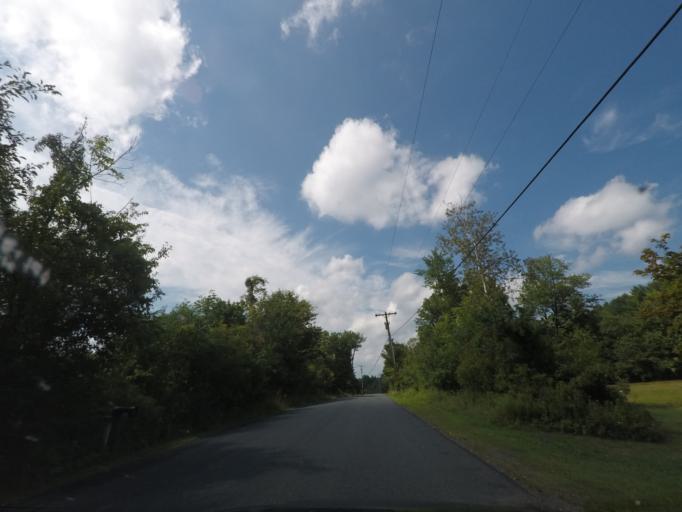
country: US
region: New York
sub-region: Rensselaer County
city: Averill Park
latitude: 42.5832
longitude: -73.5463
